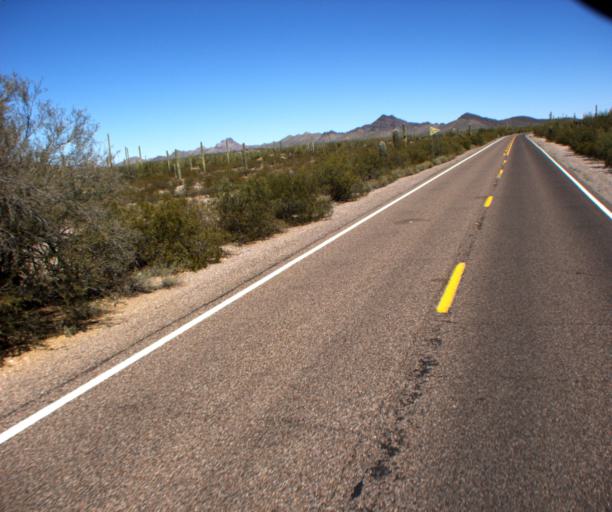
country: MX
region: Sonora
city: Sonoyta
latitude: 31.9040
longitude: -112.8111
